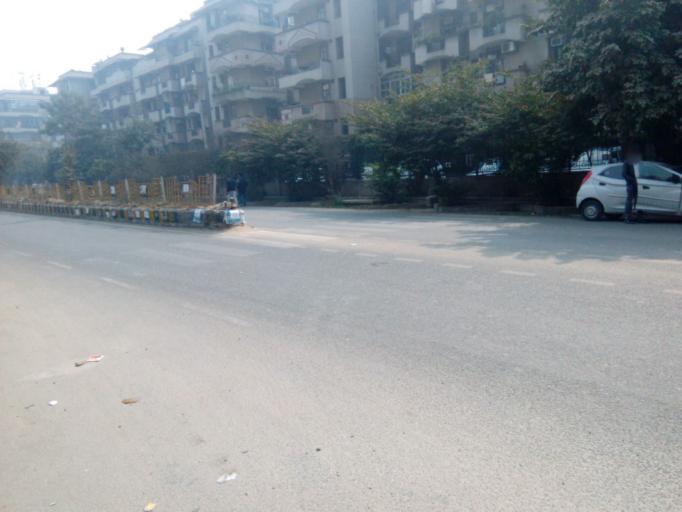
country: IN
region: Uttar Pradesh
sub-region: Gautam Buddha Nagar
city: Noida
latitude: 28.6342
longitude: 77.3644
